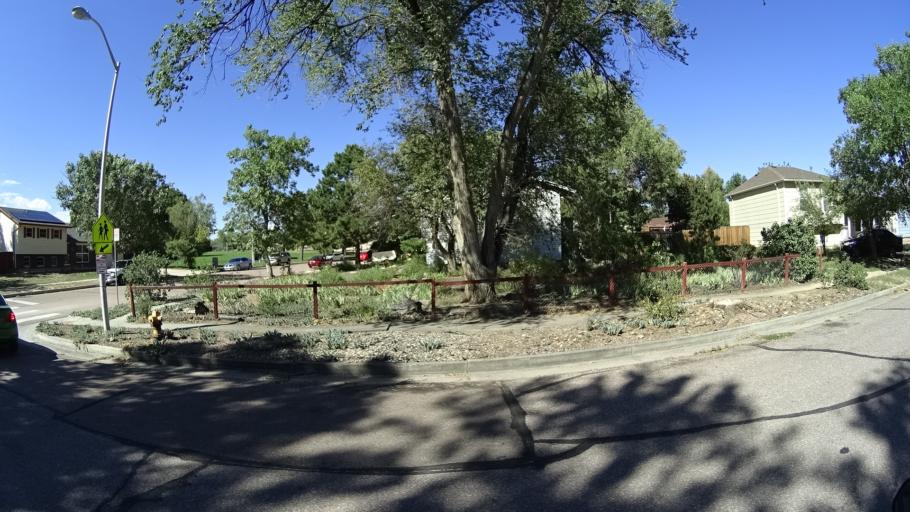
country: US
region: Colorado
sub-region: El Paso County
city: Stratmoor
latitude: 38.7908
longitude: -104.7506
